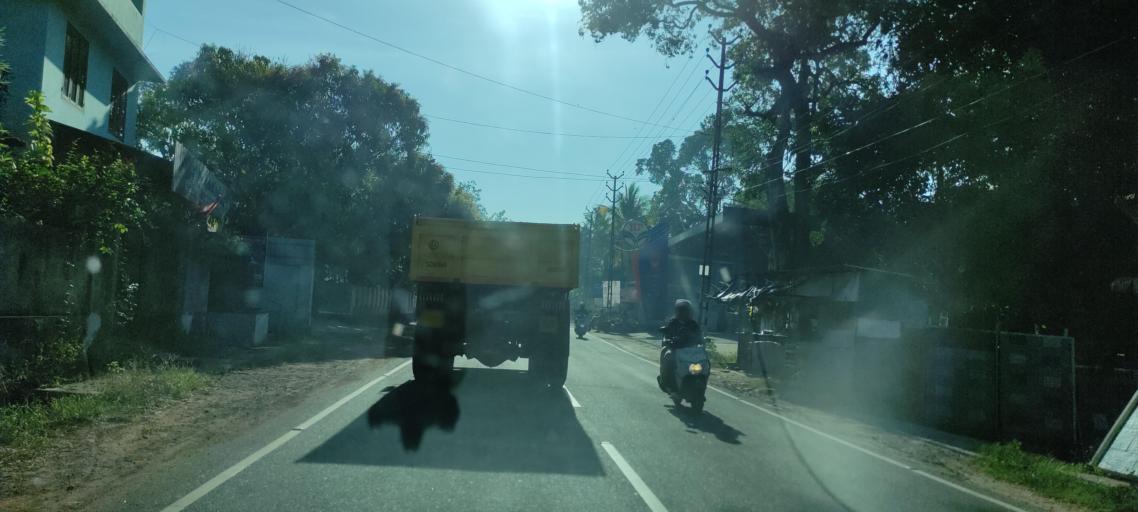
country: IN
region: Kerala
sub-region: Alappuzha
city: Kattanam
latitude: 9.1729
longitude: 76.5932
